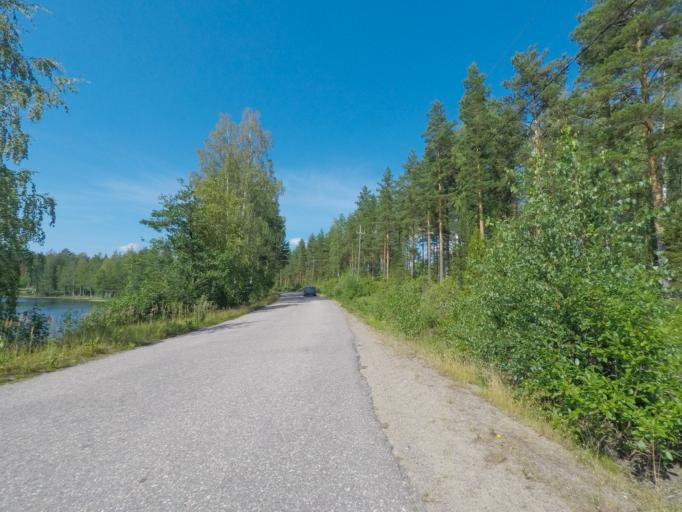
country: FI
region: Southern Savonia
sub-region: Mikkeli
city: Puumala
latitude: 61.4347
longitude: 28.1706
